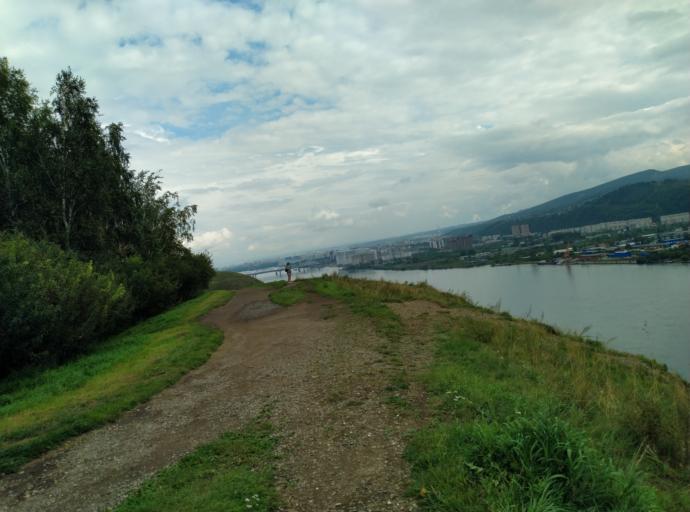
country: RU
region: Krasnoyarskiy
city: Krasnoyarsk
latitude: 55.9828
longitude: 92.7592
